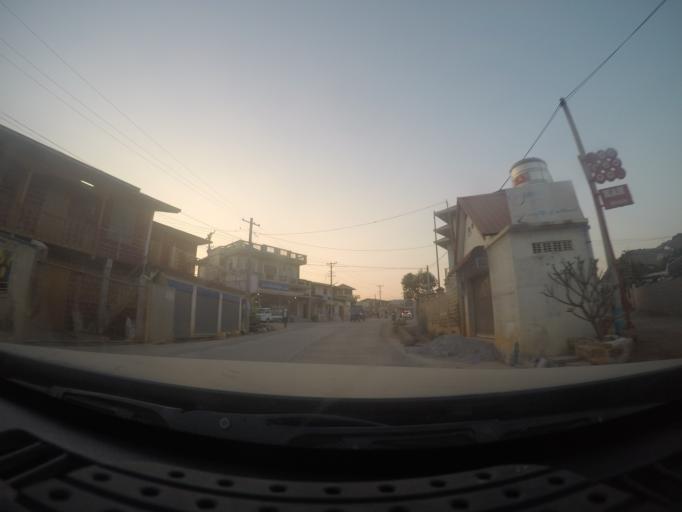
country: MM
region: Shan
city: Taunggyi
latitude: 20.7337
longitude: 97.0541
